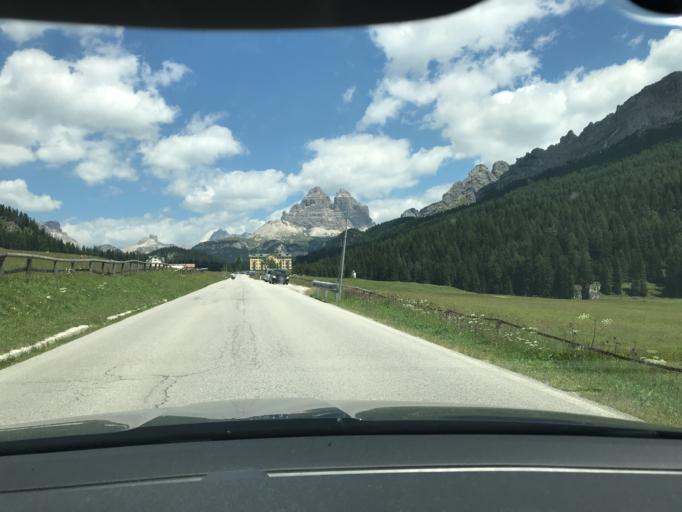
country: IT
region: Veneto
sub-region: Provincia di Belluno
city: Cortina d'Ampezzo
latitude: 46.5732
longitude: 12.2480
